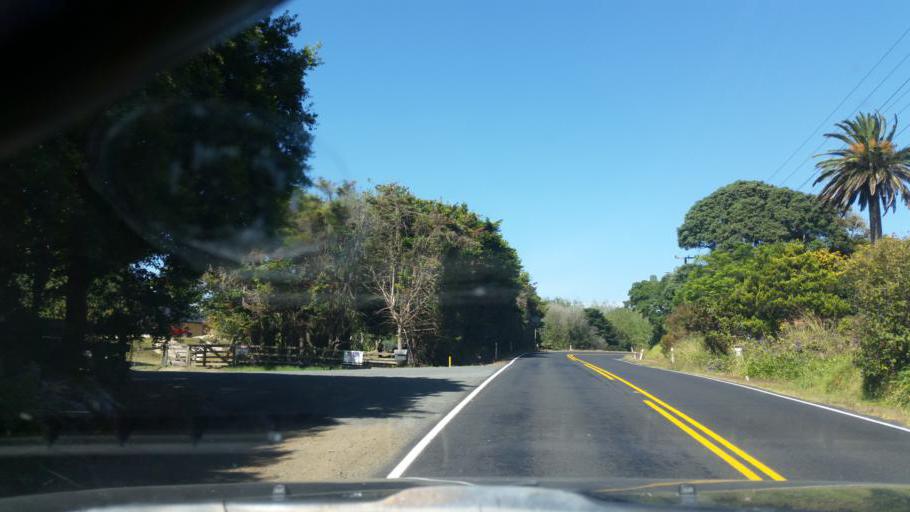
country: NZ
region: Northland
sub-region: Kaipara District
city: Dargaville
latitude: -35.9495
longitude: 173.8449
